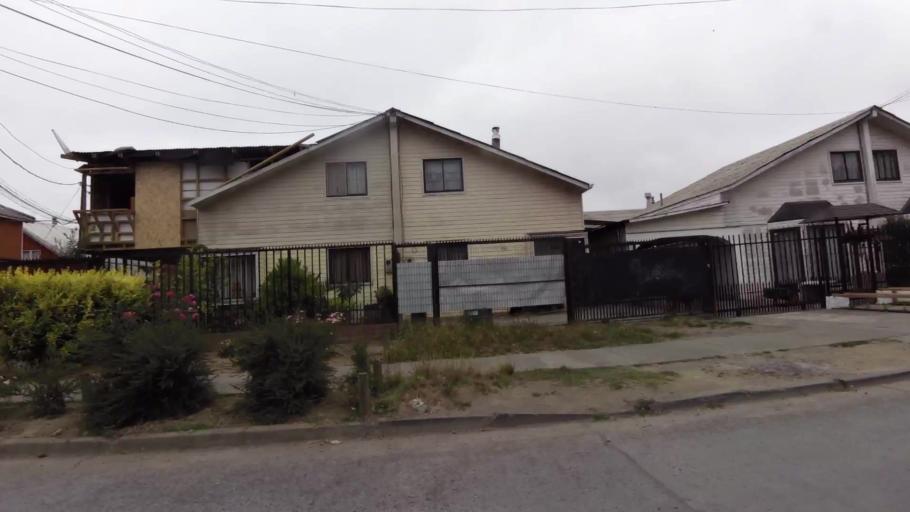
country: CL
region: Biobio
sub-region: Provincia de Concepcion
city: Concepcion
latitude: -36.8323
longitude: -73.0102
